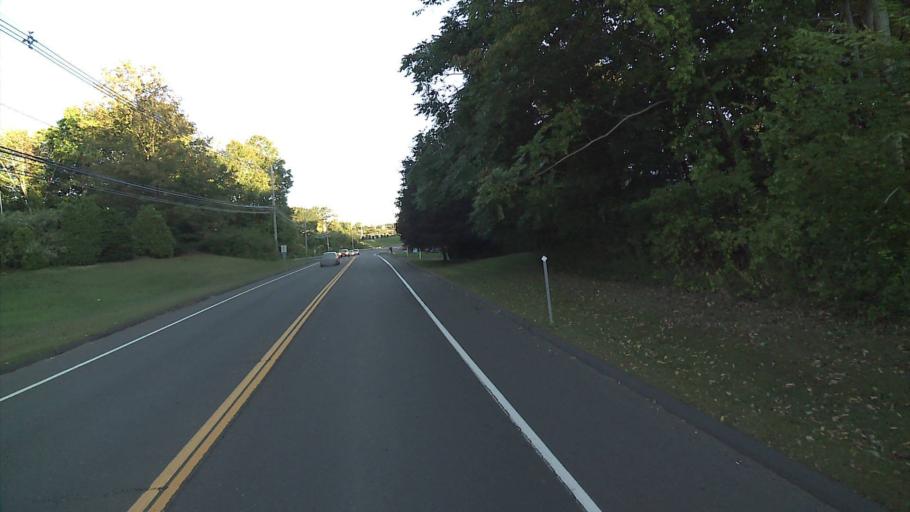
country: US
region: Connecticut
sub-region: New Haven County
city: Wallingford Center
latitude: 41.4756
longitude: -72.7639
